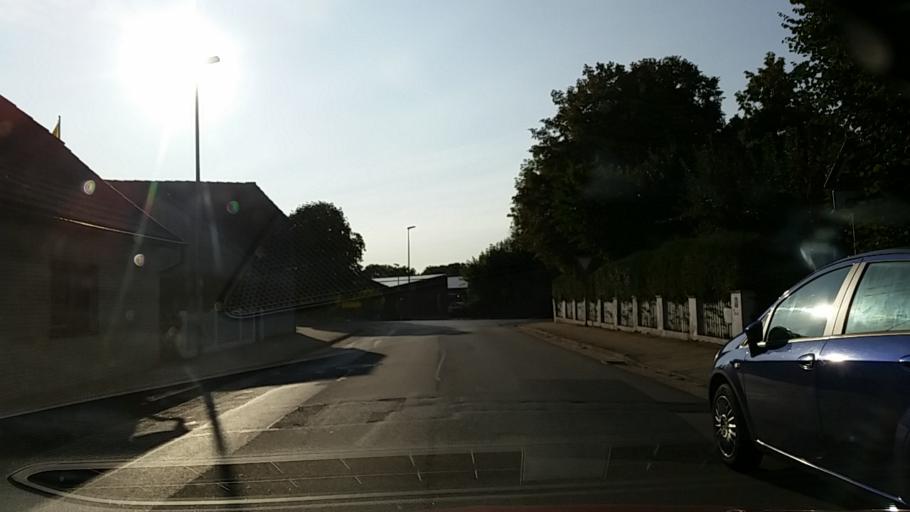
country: DE
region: Lower Saxony
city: Lehre
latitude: 52.3171
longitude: 10.6340
